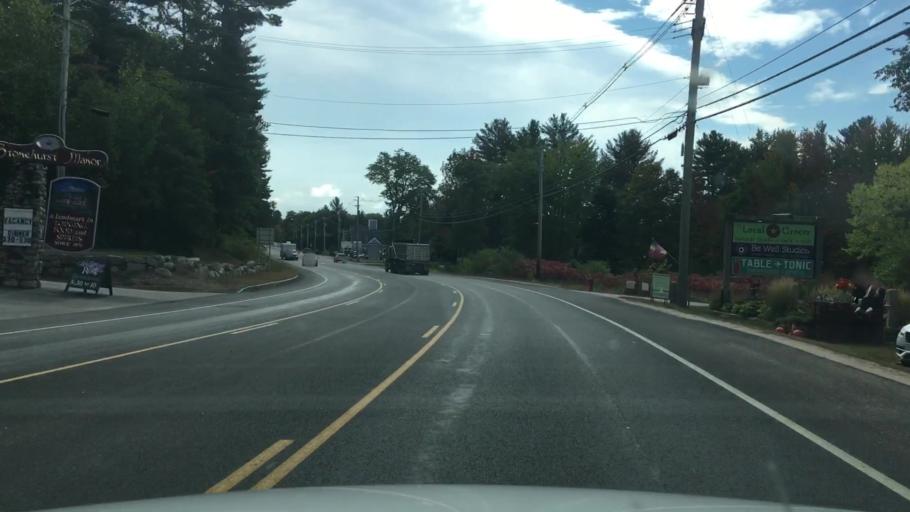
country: US
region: New Hampshire
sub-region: Carroll County
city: North Conway
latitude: 44.0679
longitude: -71.1432
